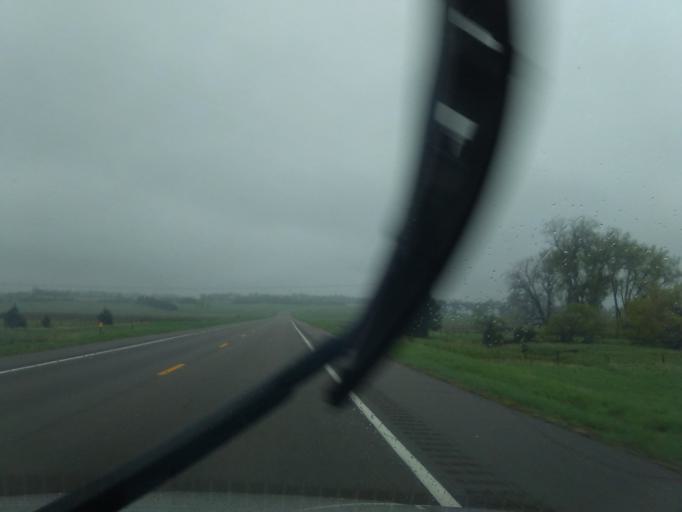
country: US
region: Nebraska
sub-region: Madison County
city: Norfolk
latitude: 42.0855
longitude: -97.3236
